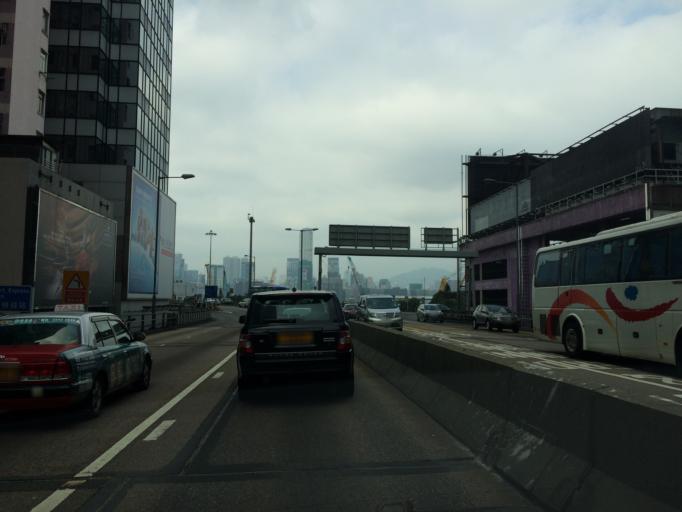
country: HK
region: Wanchai
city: Wan Chai
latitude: 22.2802
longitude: 114.1809
